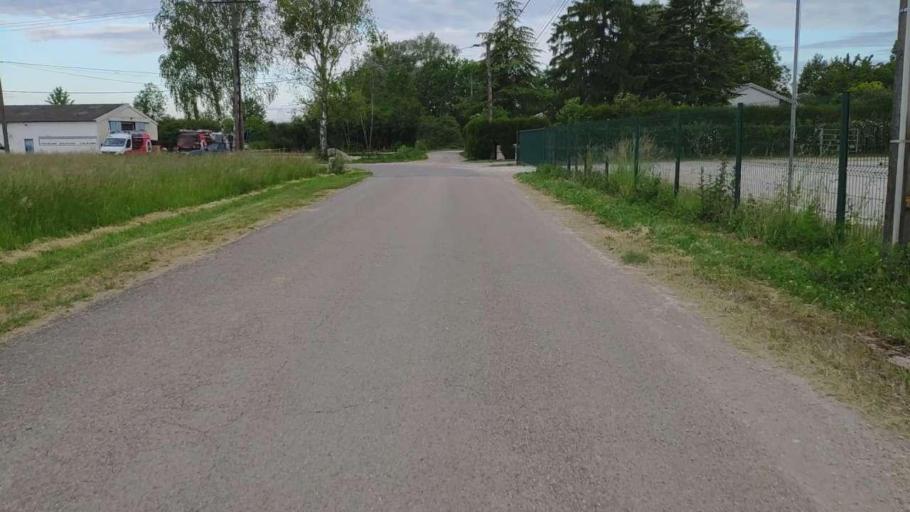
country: FR
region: Franche-Comte
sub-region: Departement du Jura
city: Bletterans
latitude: 46.7506
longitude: 5.4674
